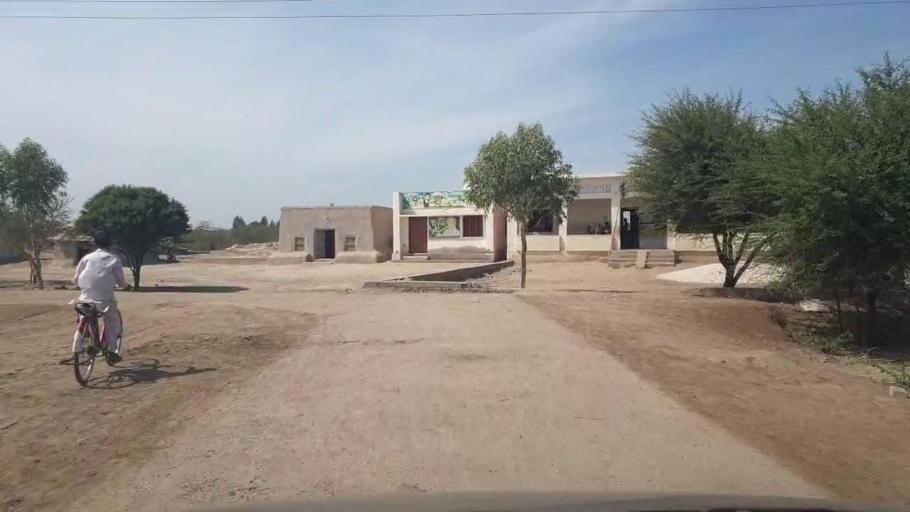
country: PK
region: Sindh
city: Kunri
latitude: 25.3342
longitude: 69.5794
